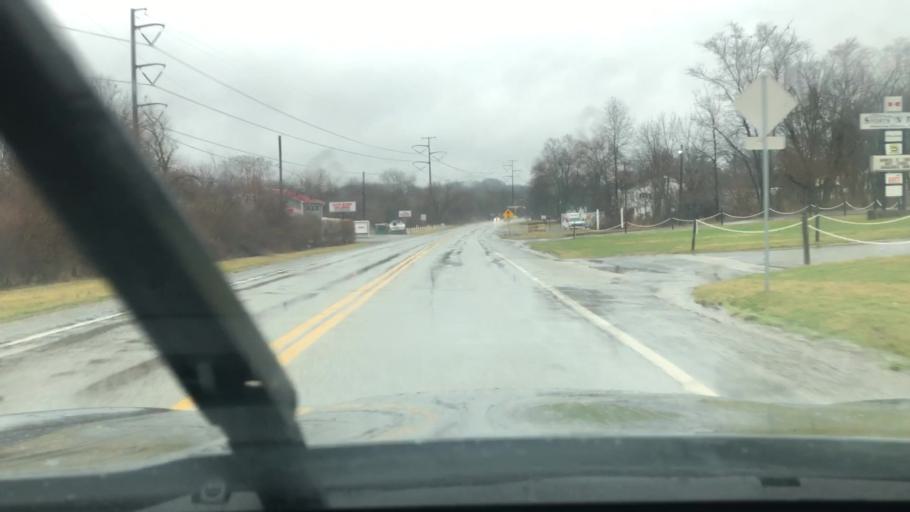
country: US
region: Pennsylvania
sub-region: Montgomery County
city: Sanatoga
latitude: 40.2029
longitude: -75.5868
